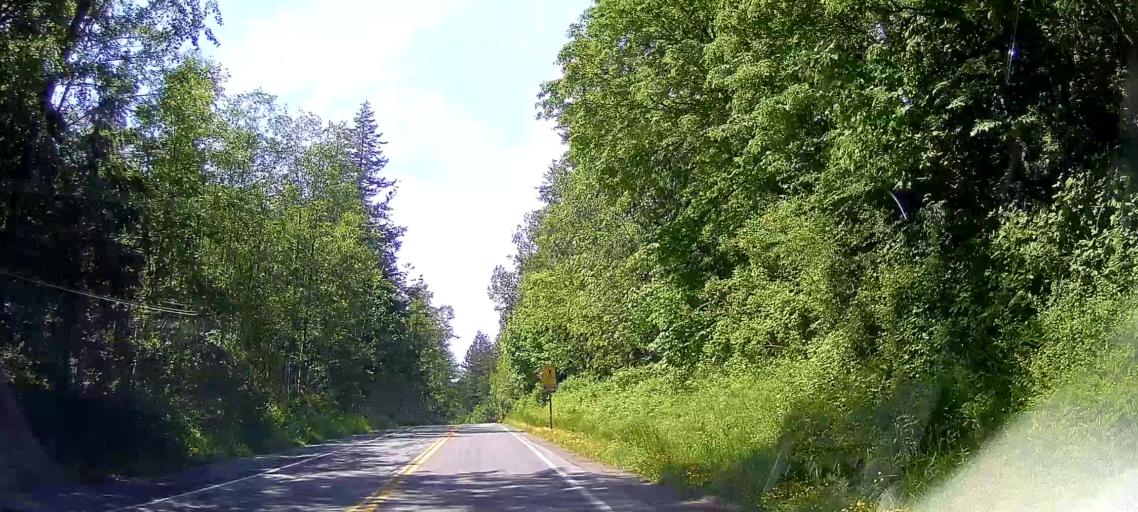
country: US
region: Washington
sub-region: Skagit County
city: Mount Vernon
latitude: 48.3975
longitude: -122.2934
